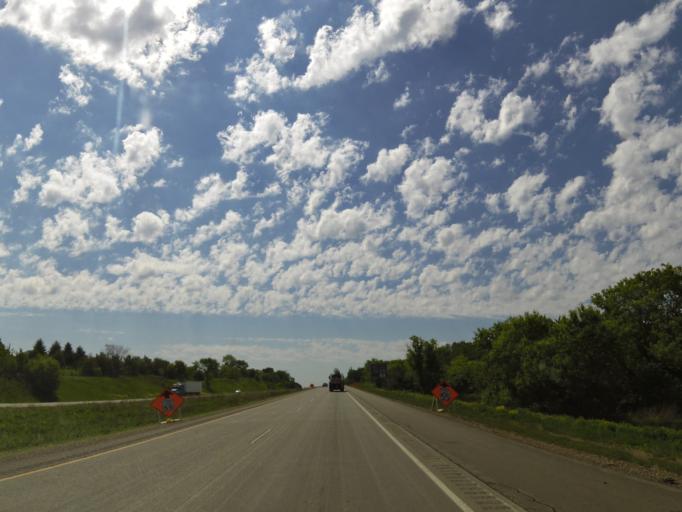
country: US
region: Wisconsin
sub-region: Eau Claire County
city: Eau Claire
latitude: 44.8065
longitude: -91.5588
